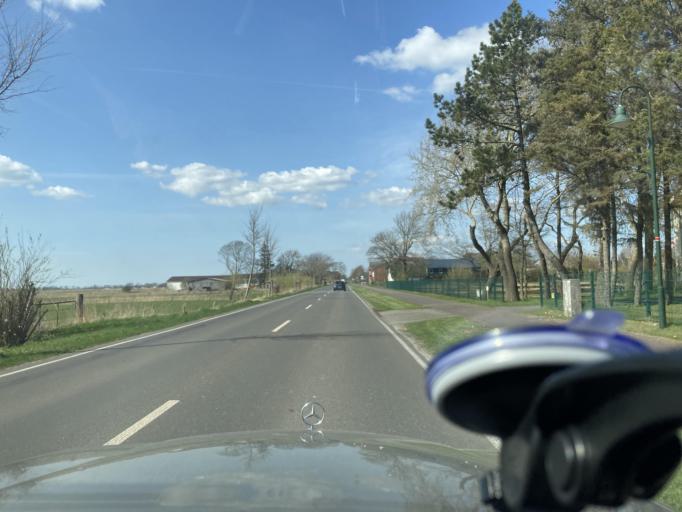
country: DE
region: Schleswig-Holstein
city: Krempel
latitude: 54.3149
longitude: 9.0307
